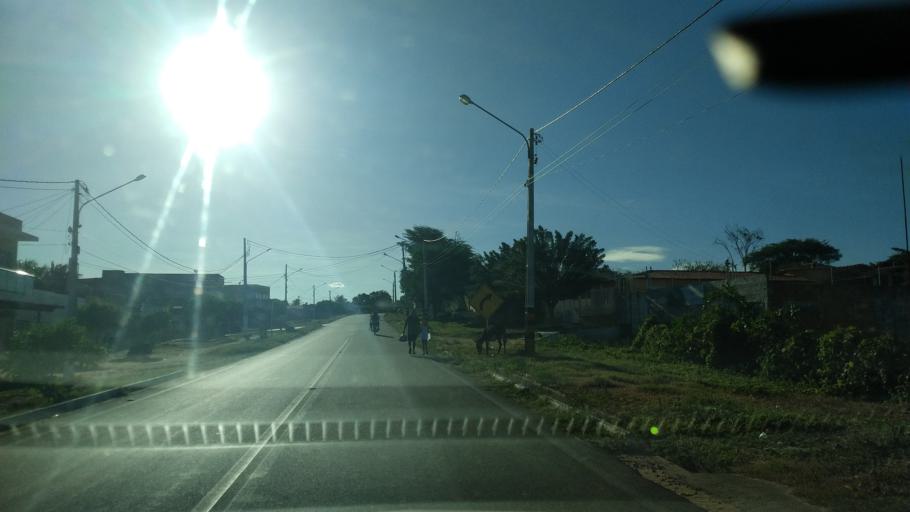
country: BR
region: Rio Grande do Norte
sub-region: Sao Jose Do Campestre
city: Sao Jose do Campestre
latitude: -6.3136
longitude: -35.7139
